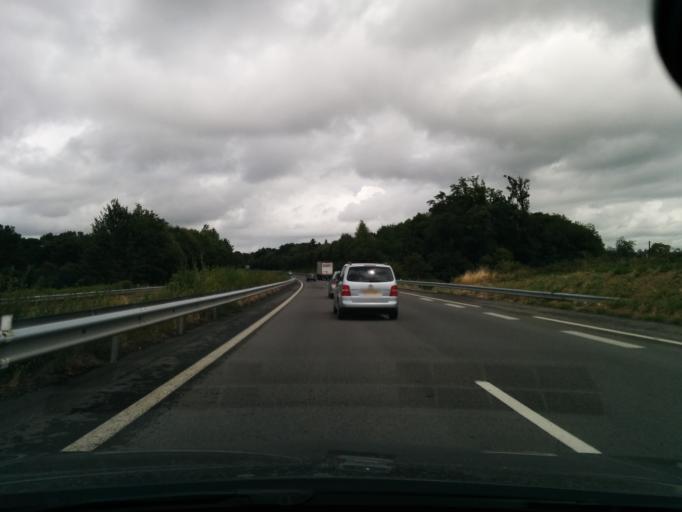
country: FR
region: Limousin
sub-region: Departement de la Correze
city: Uzerche
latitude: 45.4863
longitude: 1.5290
